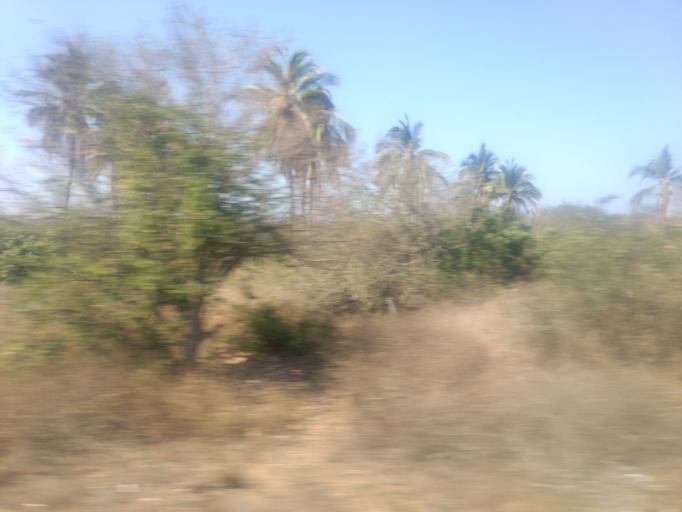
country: MX
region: Colima
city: El Colomo
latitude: 18.9914
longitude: -104.2269
